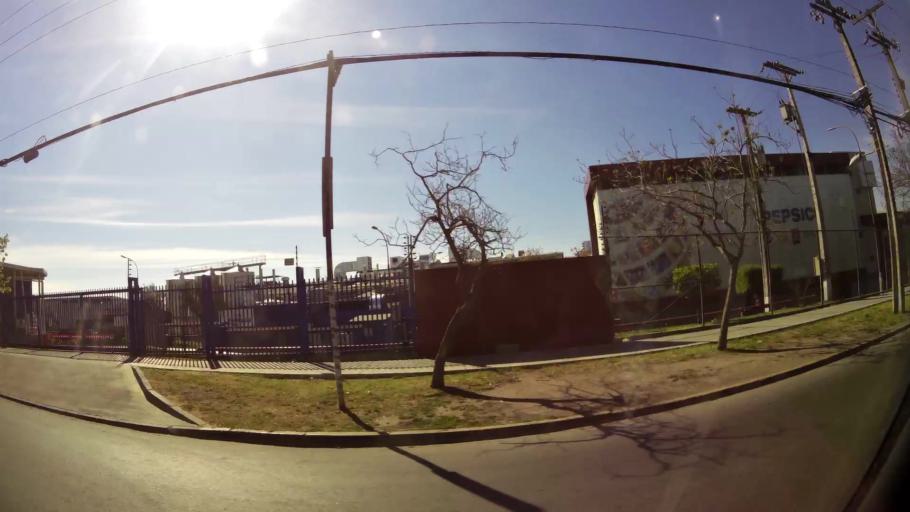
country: CL
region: Santiago Metropolitan
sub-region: Provincia de Santiago
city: Lo Prado
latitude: -33.4909
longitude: -70.7187
